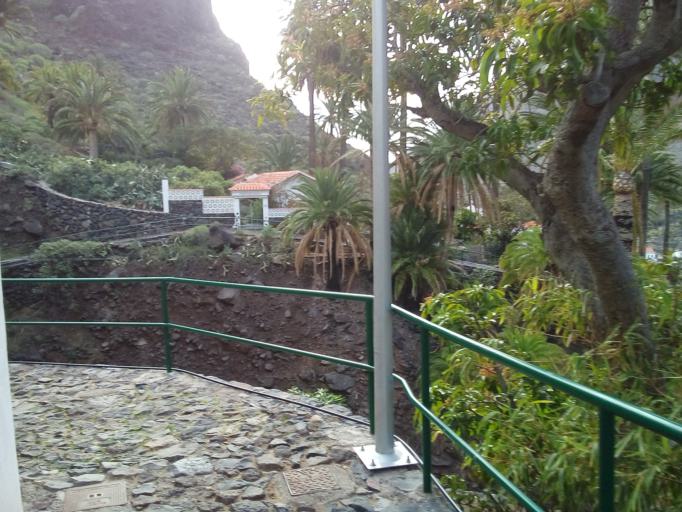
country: ES
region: Canary Islands
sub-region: Provincia de Santa Cruz de Tenerife
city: Vallehermosa
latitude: 28.1066
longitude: -17.3227
